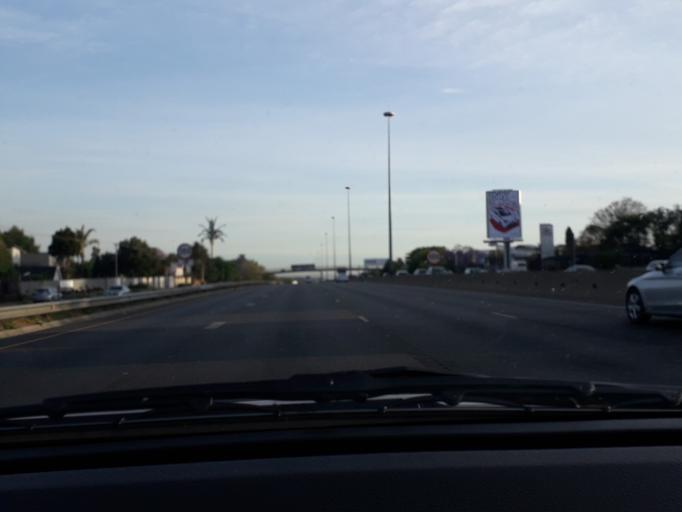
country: ZA
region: Gauteng
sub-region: City of Johannesburg Metropolitan Municipality
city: Modderfontein
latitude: -26.0860
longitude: 28.0862
